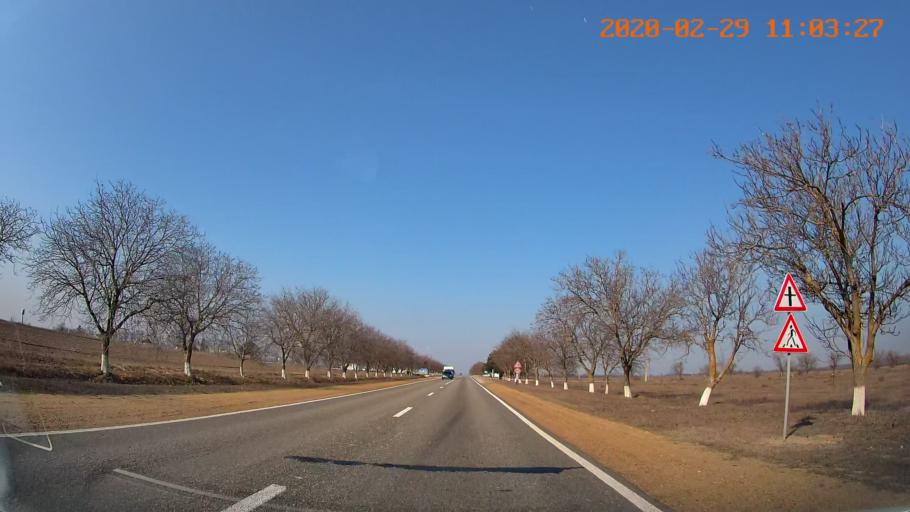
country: MD
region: Criuleni
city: Criuleni
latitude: 47.1797
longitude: 29.2171
